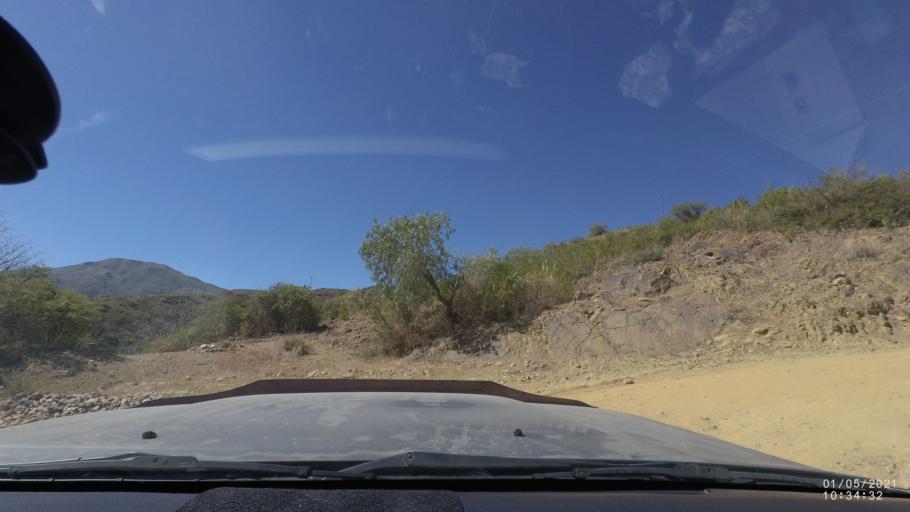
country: BO
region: Cochabamba
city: Capinota
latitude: -17.5971
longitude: -66.1901
